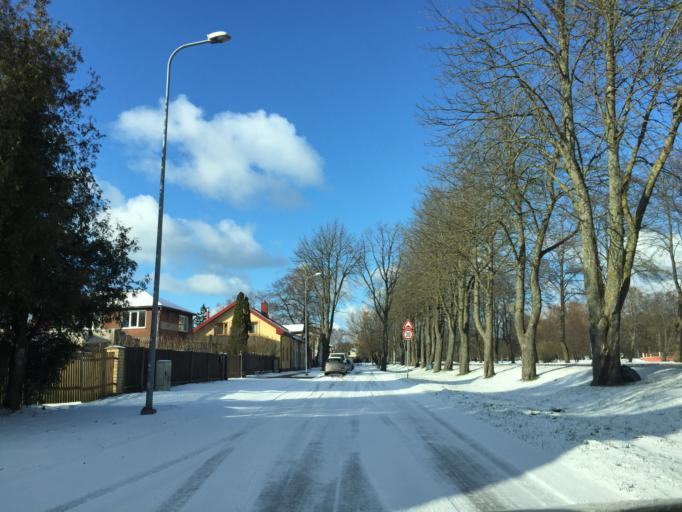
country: LV
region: Ventspils
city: Ventspils
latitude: 57.3826
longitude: 21.5661
